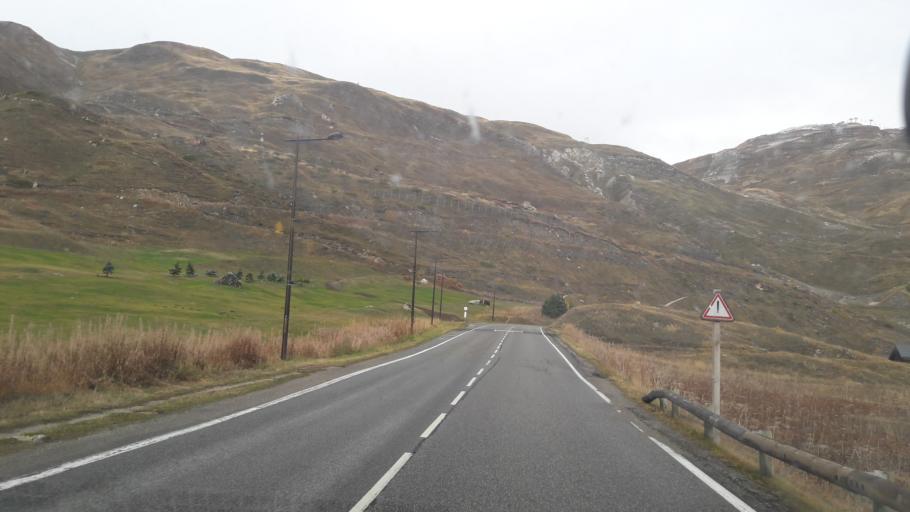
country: FR
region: Rhone-Alpes
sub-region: Departement de la Savoie
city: Tignes
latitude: 45.4619
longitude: 6.9001
